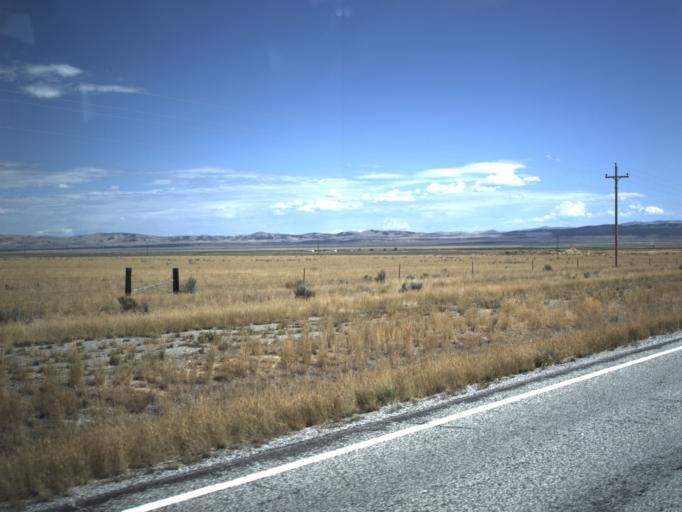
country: US
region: Idaho
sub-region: Oneida County
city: Malad City
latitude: 41.9659
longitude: -112.9850
